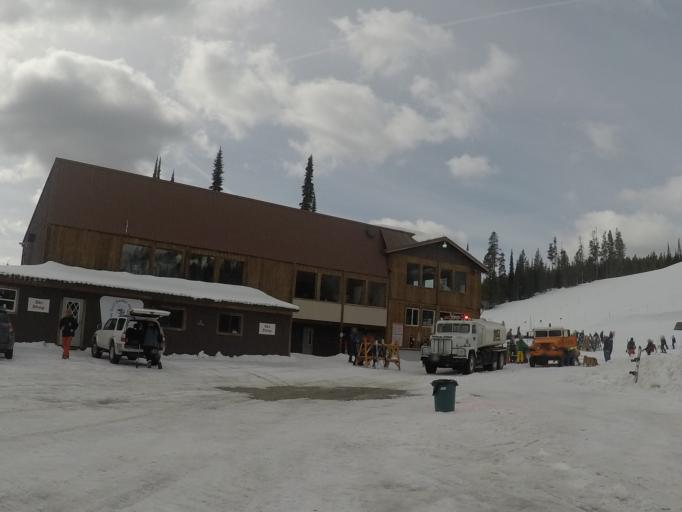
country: US
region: Idaho
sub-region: Lemhi County
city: Salmon
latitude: 45.6923
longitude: -113.9522
